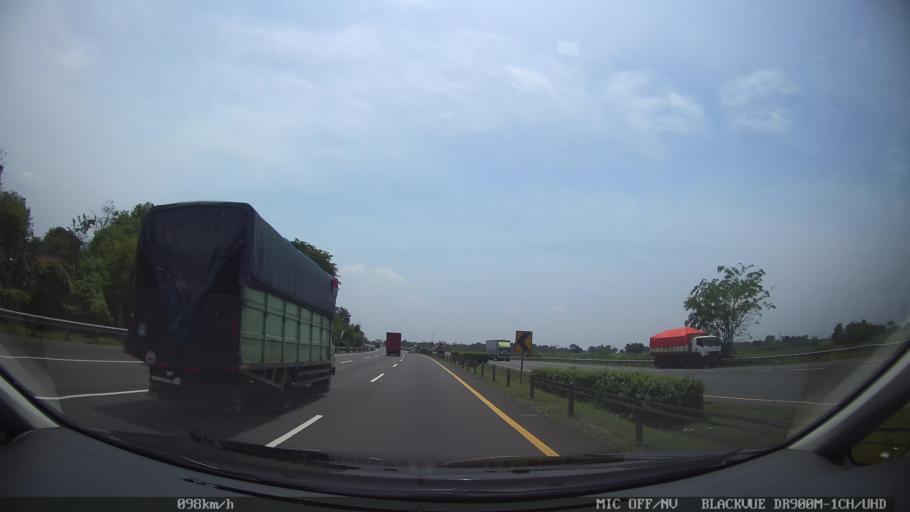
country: ID
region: West Java
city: Kresek
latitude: -6.1857
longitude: 106.4064
